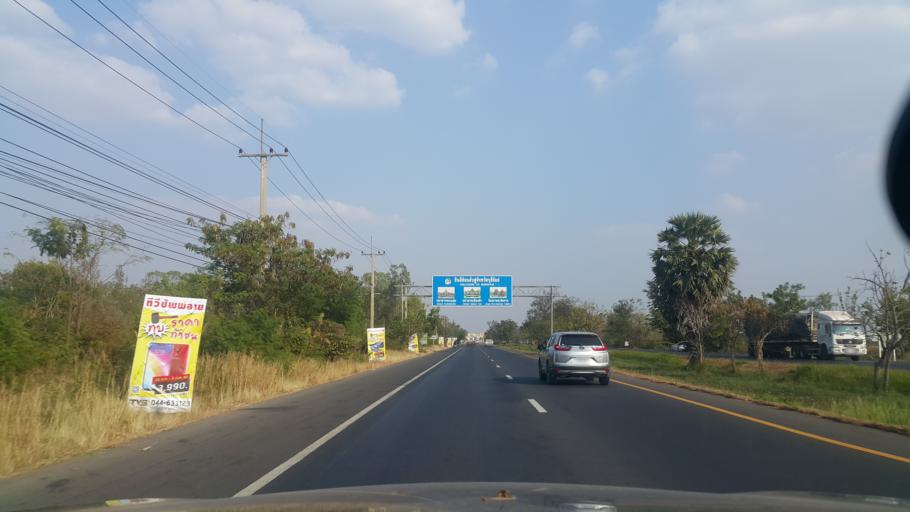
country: TH
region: Buriram
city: Nang Rong
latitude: 14.6368
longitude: 102.7657
